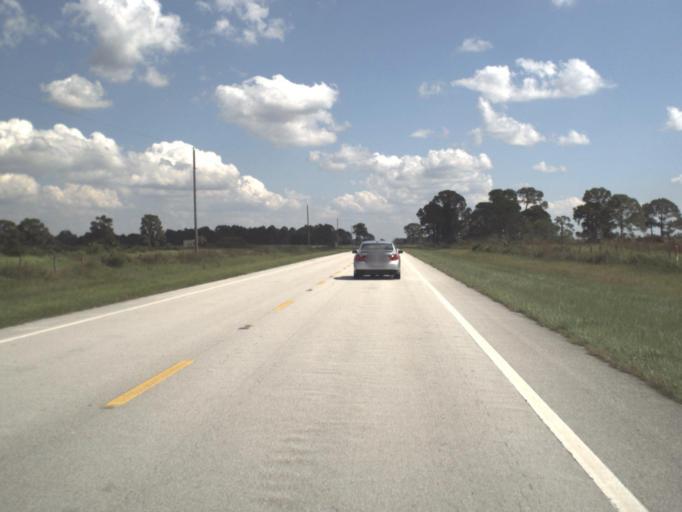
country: US
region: Florida
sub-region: Highlands County
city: Lake Placid
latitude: 27.3740
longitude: -81.0892
